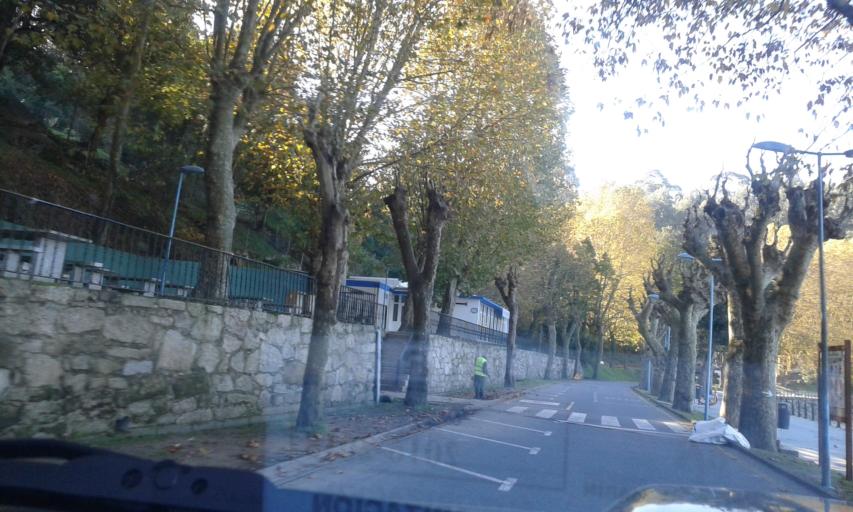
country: ES
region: Galicia
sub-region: Provincia de Pontevedra
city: Marin
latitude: 42.3904
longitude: -8.7141
